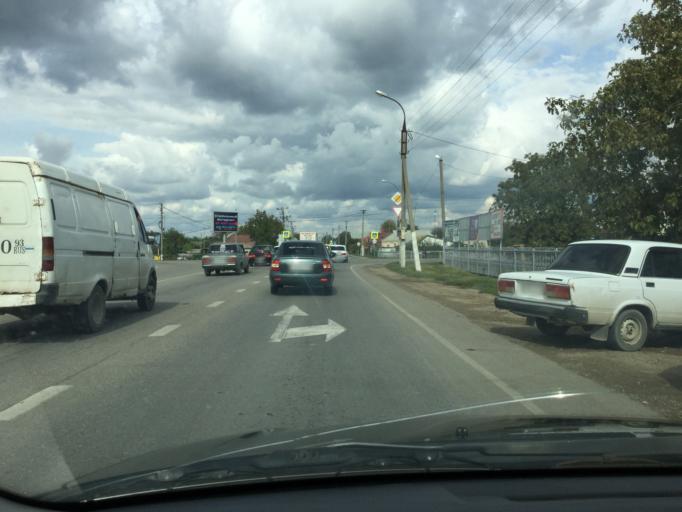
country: RU
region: Krasnodarskiy
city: Slavyansk-na-Kubani
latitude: 45.2488
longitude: 38.1005
